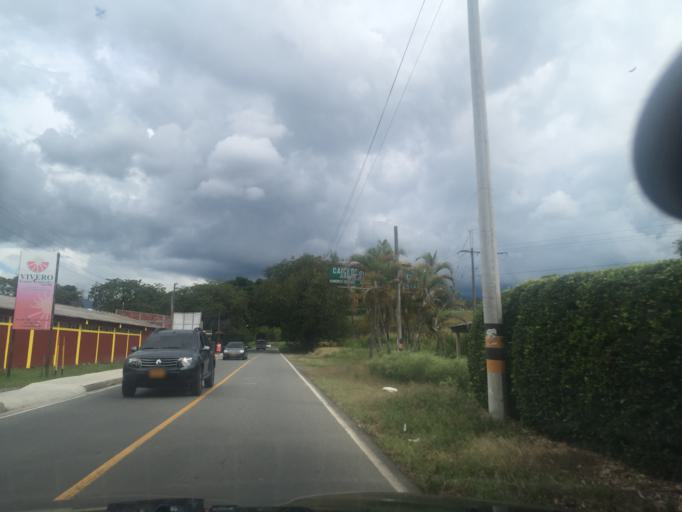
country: CO
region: Valle del Cauca
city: Caicedonia
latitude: 4.3415
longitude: -75.8480
